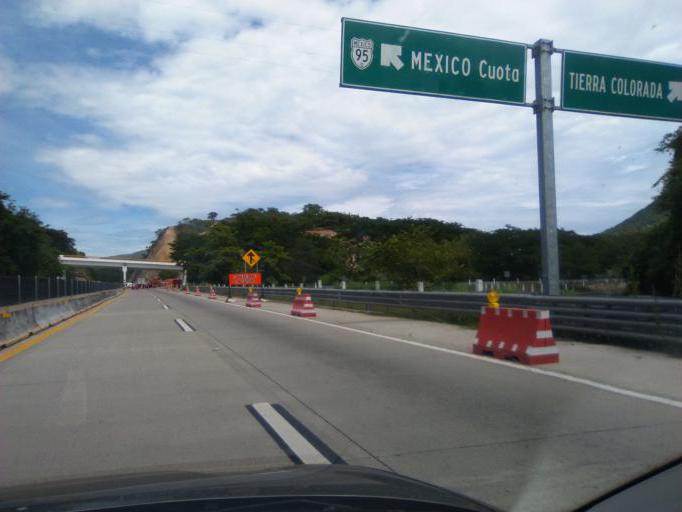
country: MX
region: Guerrero
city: Tierra Colorada
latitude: 17.1754
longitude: -99.5532
